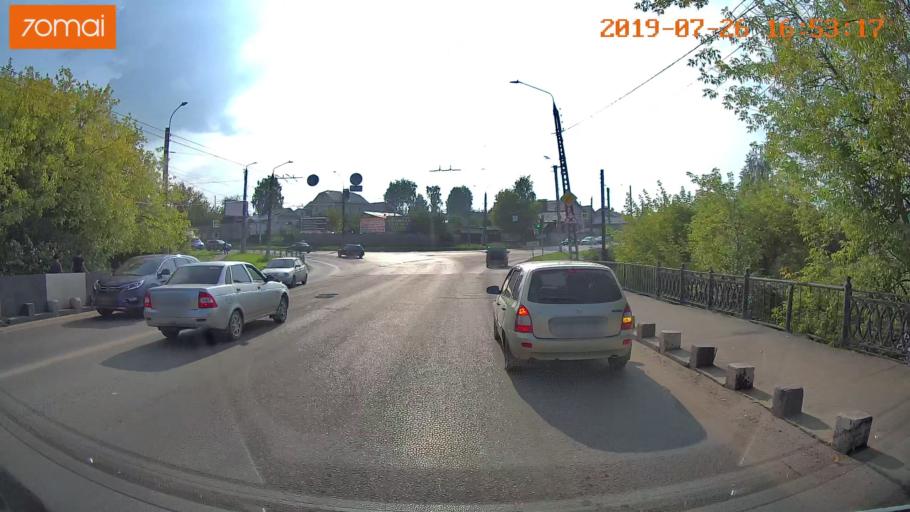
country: RU
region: Ivanovo
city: Bogorodskoye
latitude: 57.0169
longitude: 41.0035
